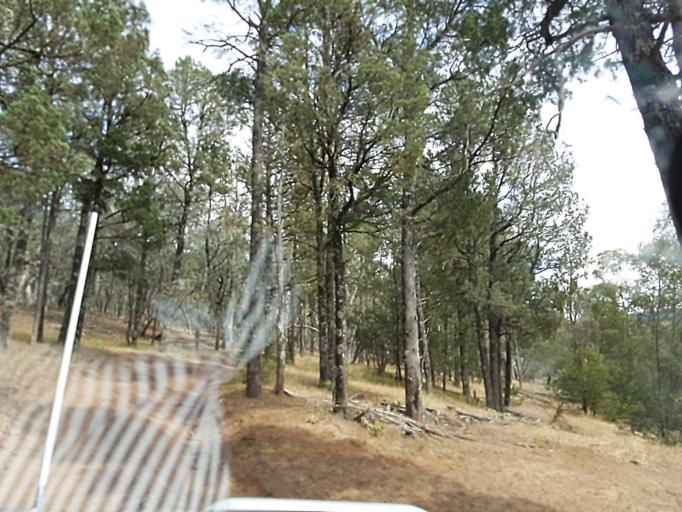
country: AU
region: New South Wales
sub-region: Snowy River
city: Jindabyne
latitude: -36.9484
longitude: 148.3977
